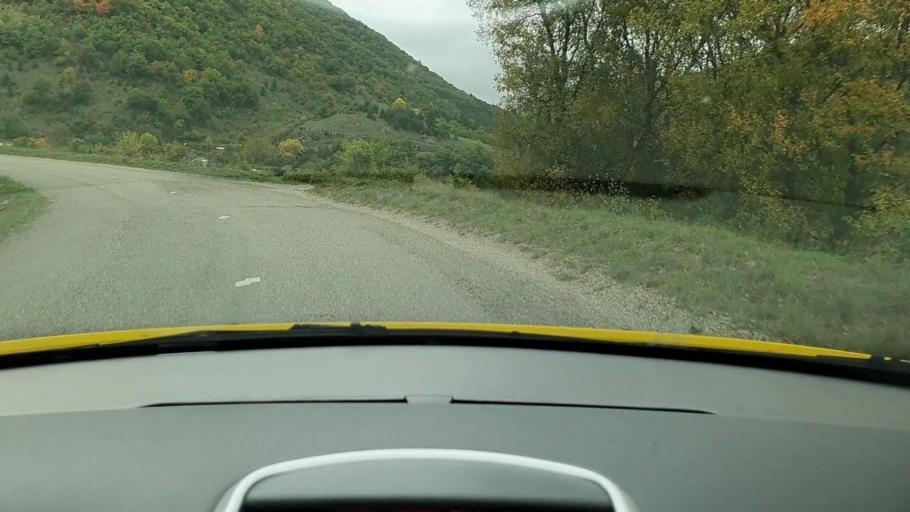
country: FR
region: Languedoc-Roussillon
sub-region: Departement de la Lozere
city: Meyrueis
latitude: 44.0753
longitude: 3.3356
